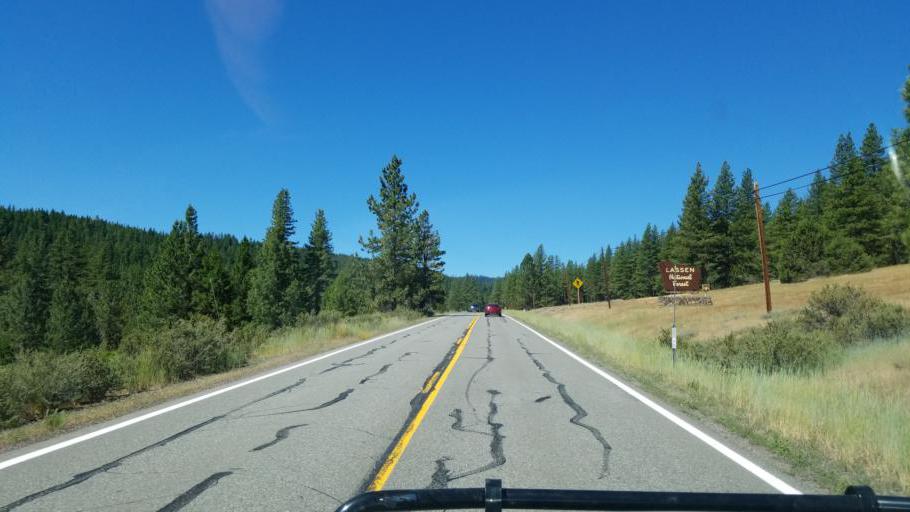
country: US
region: California
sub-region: Lassen County
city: Susanville
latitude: 40.3800
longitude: -120.8049
